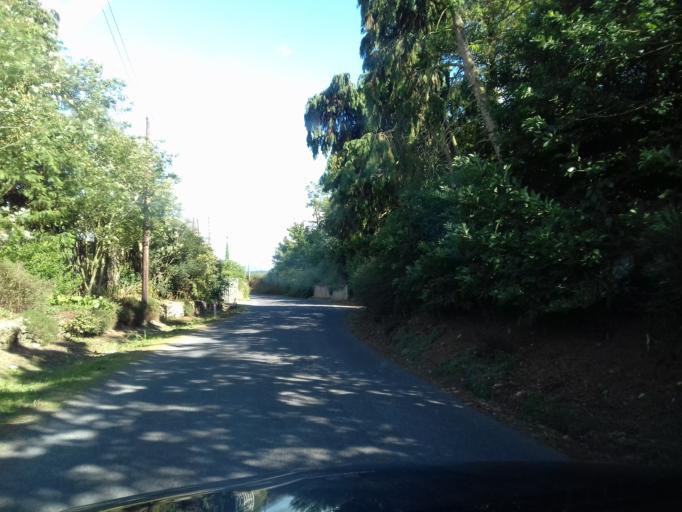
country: IE
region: Leinster
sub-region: Kilkenny
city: Callan
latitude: 52.5391
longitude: -7.3226
